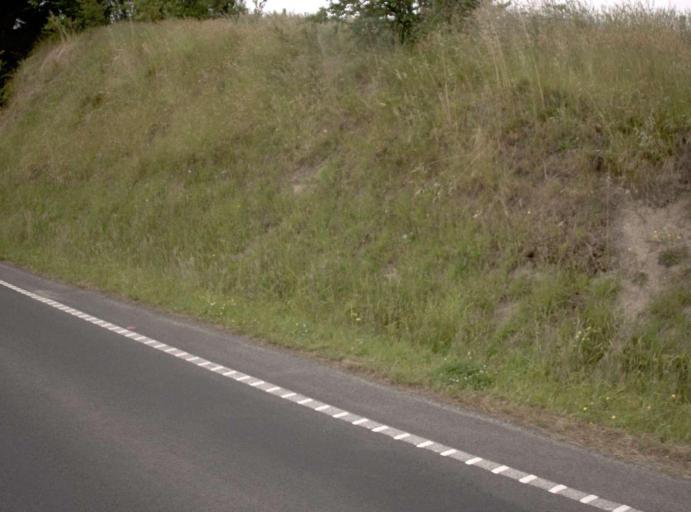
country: AU
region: Victoria
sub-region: Bass Coast
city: North Wonthaggi
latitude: -38.5557
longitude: 145.9541
